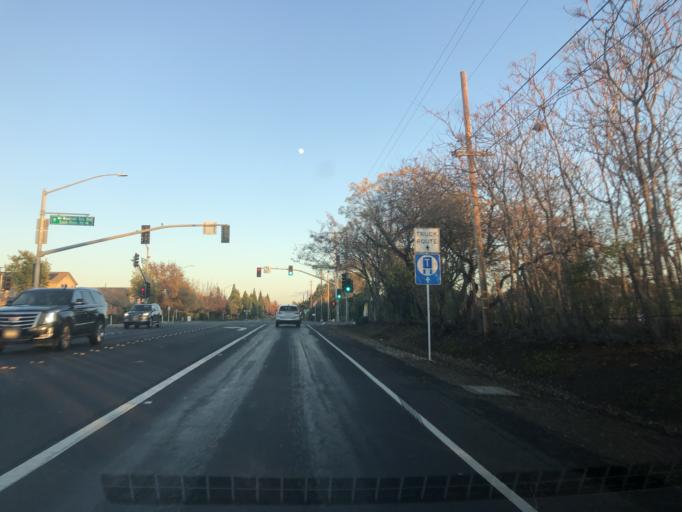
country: US
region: California
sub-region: Sacramento County
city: Antelope
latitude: 38.7518
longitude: -121.3379
